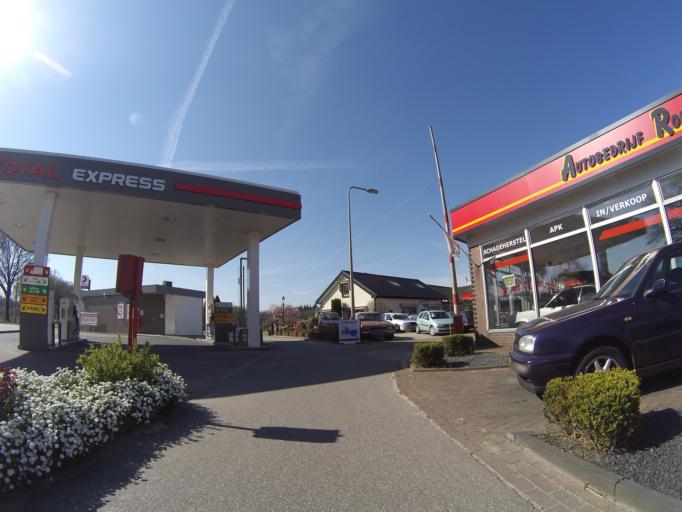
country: NL
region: Utrecht
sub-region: Gemeente Utrechtse Heuvelrug
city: Overberg
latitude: 52.0760
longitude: 5.5293
